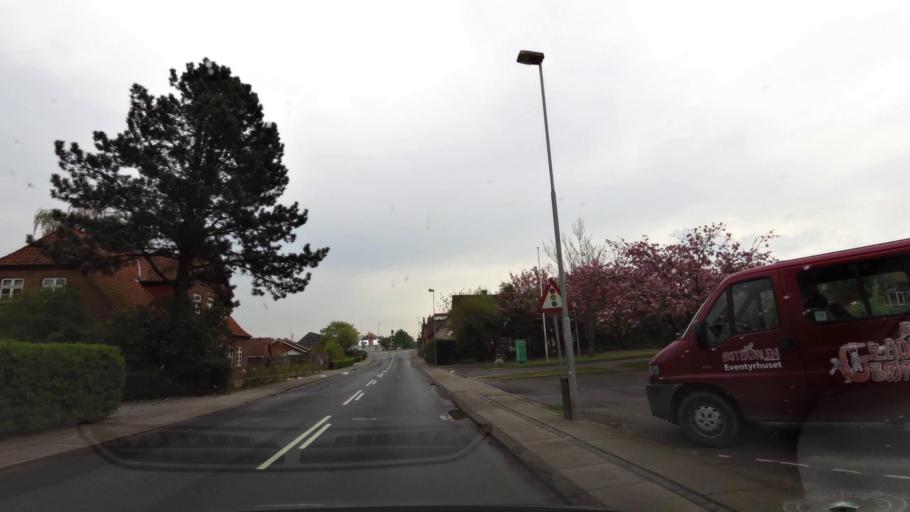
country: DK
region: South Denmark
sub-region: Svendborg Kommune
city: Thuro By
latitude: 55.1547
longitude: 10.6712
